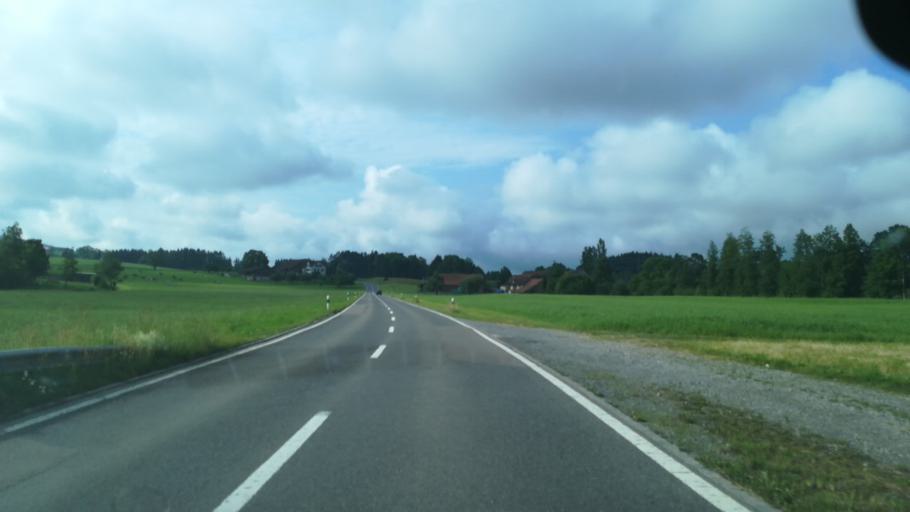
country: CH
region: Saint Gallen
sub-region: Wahlkreis St. Gallen
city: Andwil
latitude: 47.4623
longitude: 9.2481
